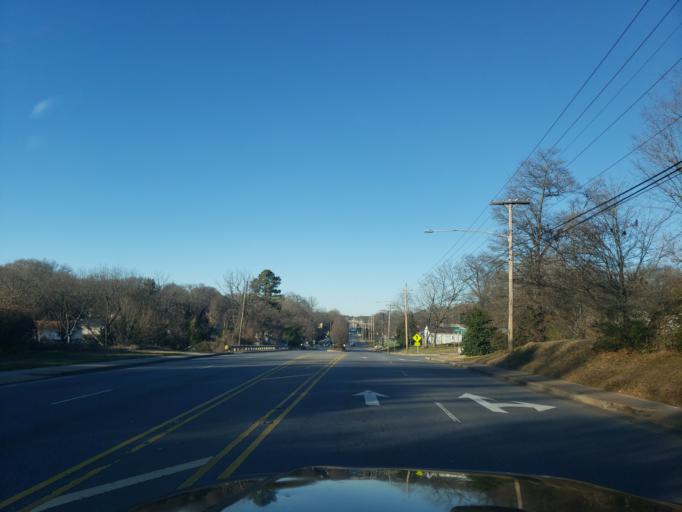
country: US
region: North Carolina
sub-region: Gaston County
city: Gastonia
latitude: 35.2710
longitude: -81.1877
